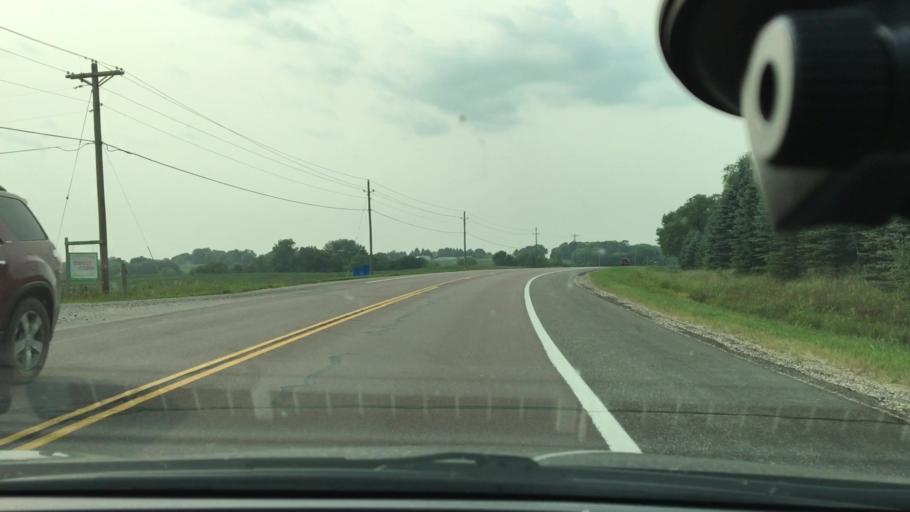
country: US
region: Minnesota
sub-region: Hennepin County
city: Dayton
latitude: 45.2456
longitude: -93.5306
